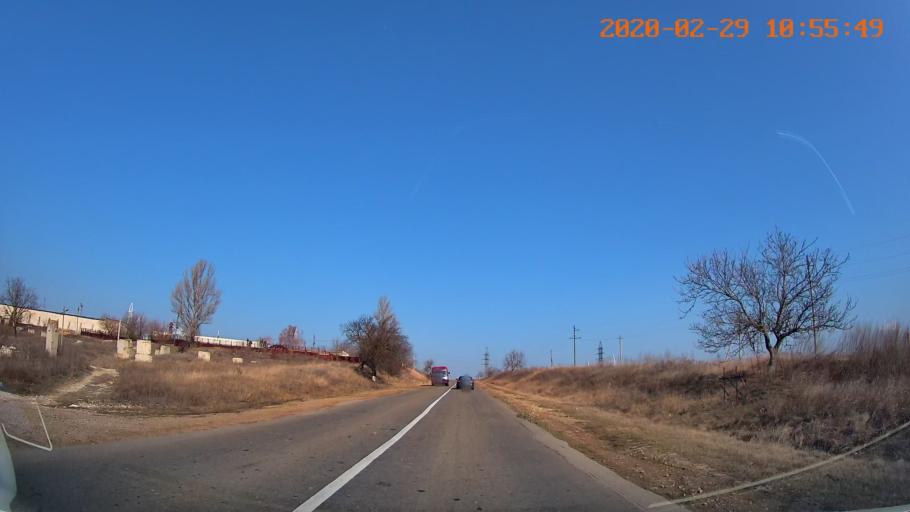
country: MD
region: Telenesti
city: Grigoriopol
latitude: 47.1383
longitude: 29.3256
